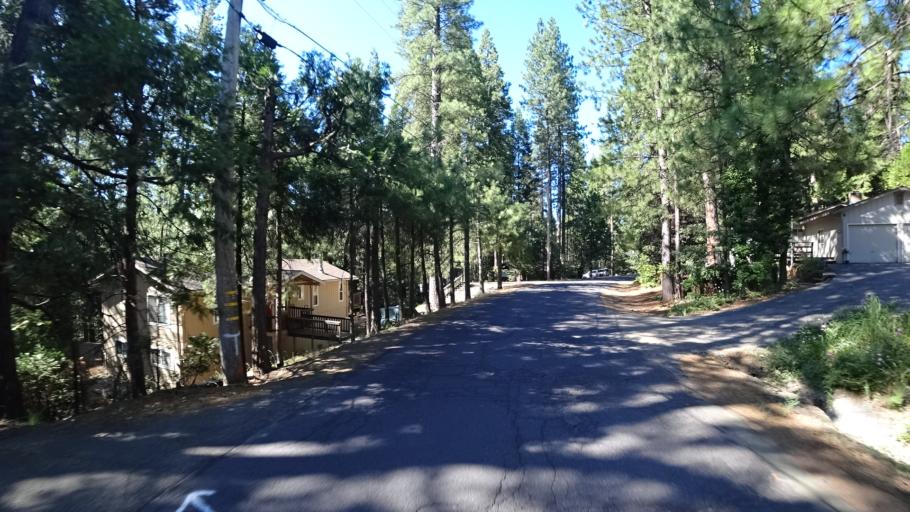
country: US
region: California
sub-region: Calaveras County
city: Arnold
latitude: 38.2438
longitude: -120.3643
